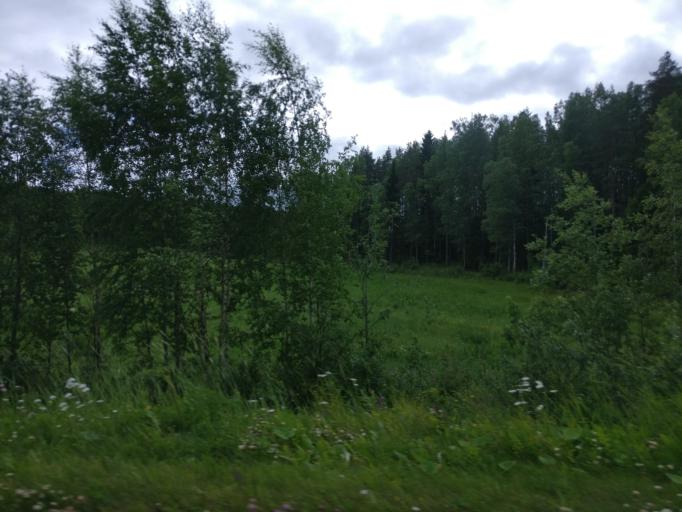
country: FI
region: Northern Savo
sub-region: Kuopio
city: Vehmersalmi
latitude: 62.9364
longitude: 27.9346
